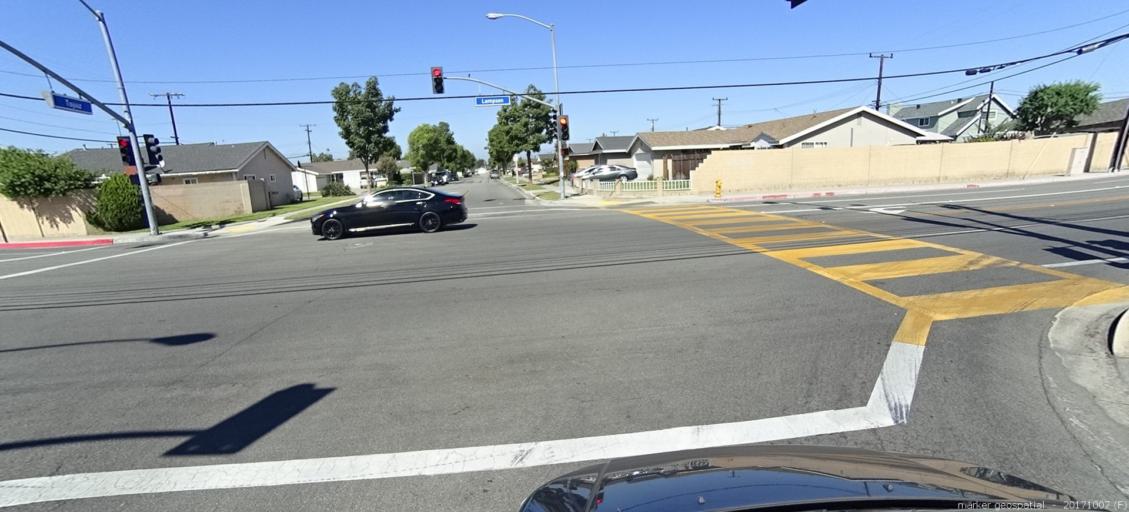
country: US
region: California
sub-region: Orange County
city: Westminster
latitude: 33.7810
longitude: -118.0238
